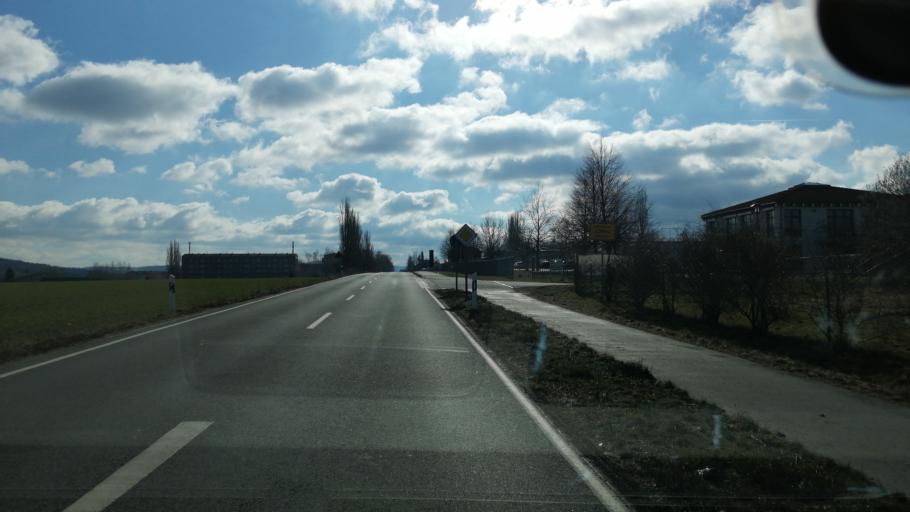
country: DE
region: Saxony
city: Lobau
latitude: 51.1118
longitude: 14.6720
